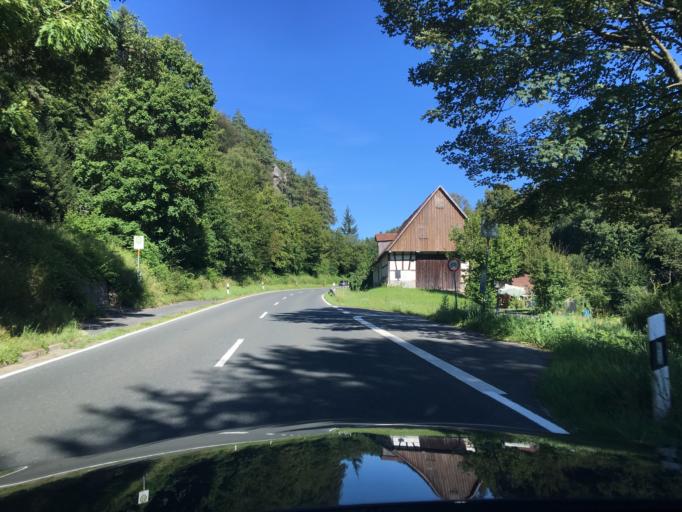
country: DE
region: Bavaria
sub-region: Upper Franconia
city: Obertrubach
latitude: 49.6900
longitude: 11.3312
